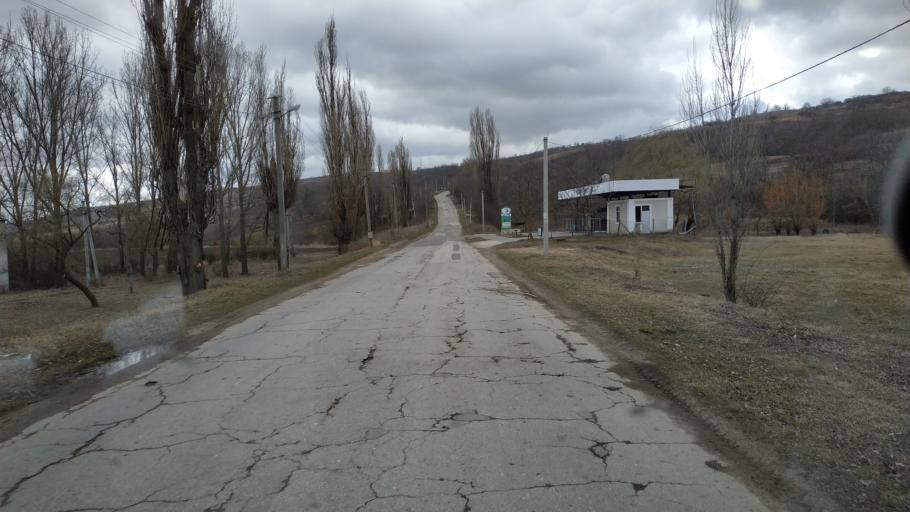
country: MD
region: Stinga Nistrului
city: Bucovat
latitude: 47.2295
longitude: 28.4263
